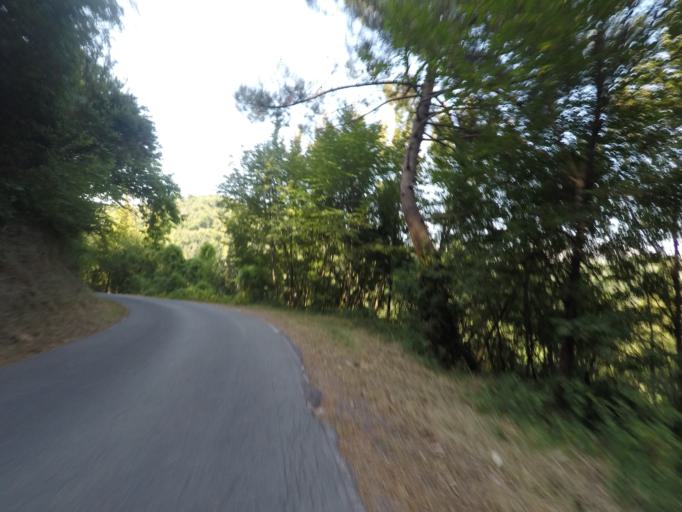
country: IT
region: Tuscany
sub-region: Provincia di Massa-Carrara
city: Carrara
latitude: 44.0836
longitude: 10.0650
